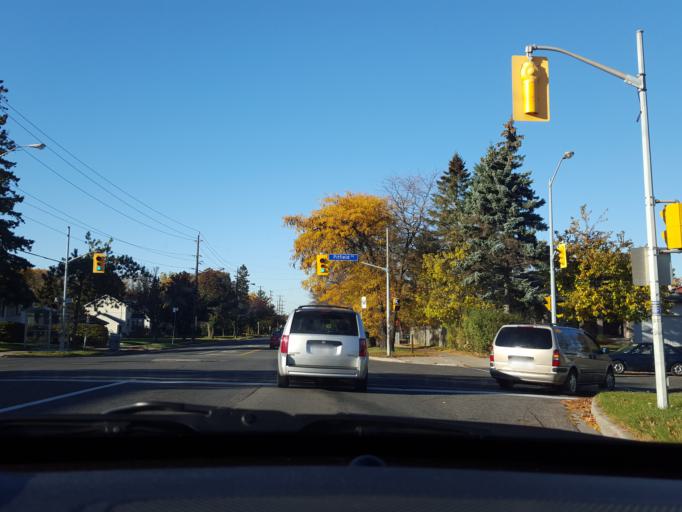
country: CA
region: Ontario
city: Scarborough
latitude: 43.7832
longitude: -79.2662
